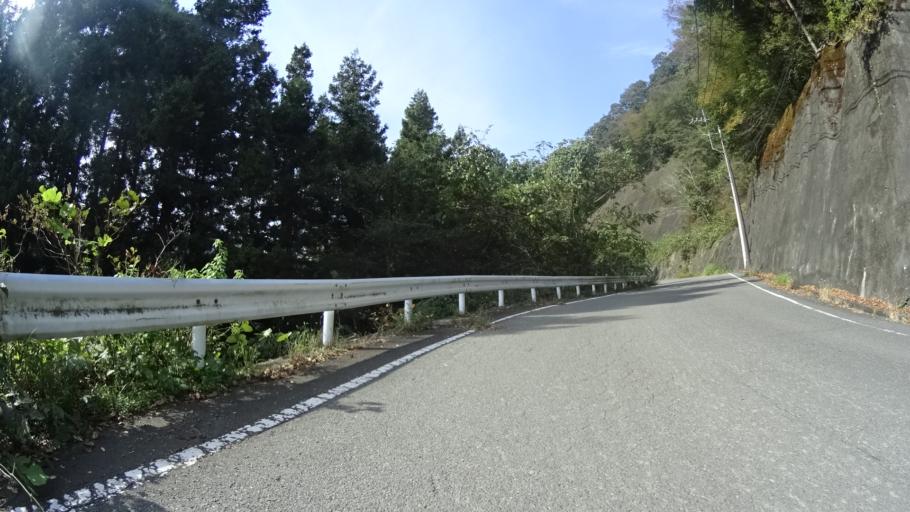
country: JP
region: Yamanashi
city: Otsuki
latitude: 35.5969
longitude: 138.9727
